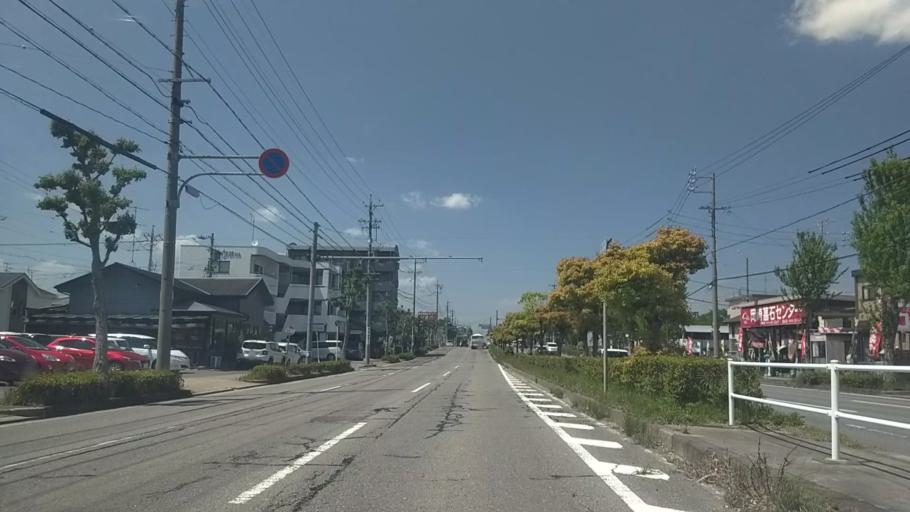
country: JP
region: Aichi
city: Okazaki
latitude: 34.9659
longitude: 137.1831
